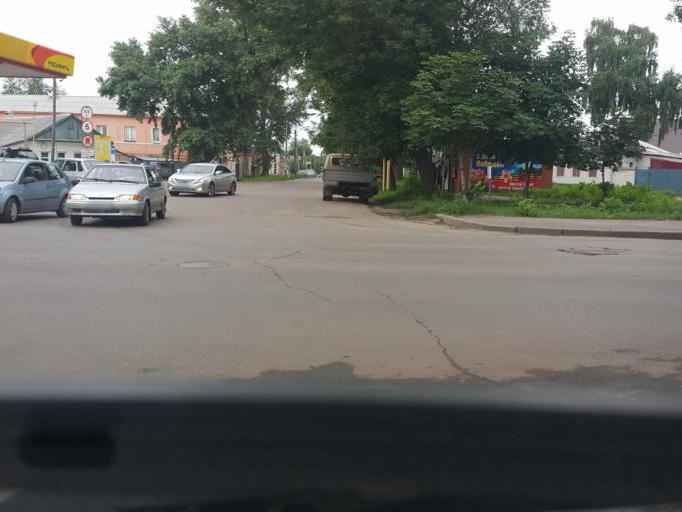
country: RU
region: Tambov
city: Michurinsk
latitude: 52.8920
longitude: 40.5034
